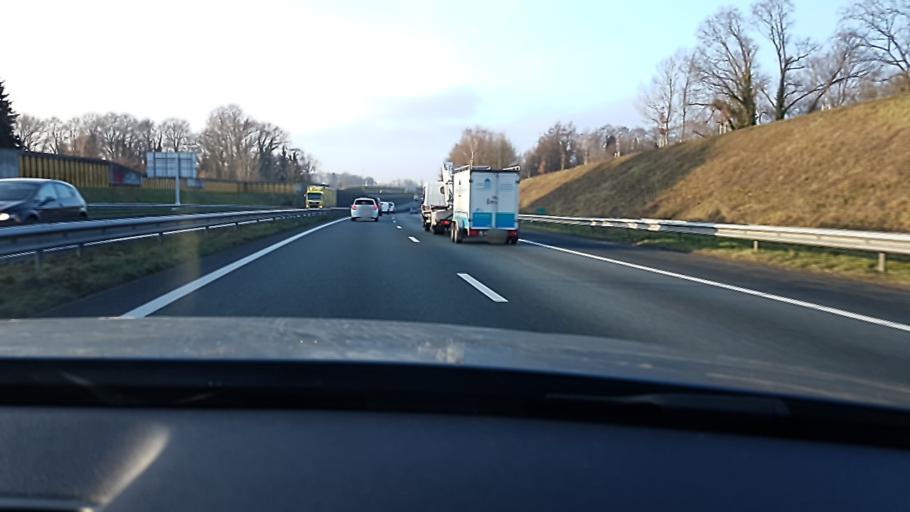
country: NL
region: Overijssel
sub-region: Gemeente Hengelo
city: Hengelo
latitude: 52.2771
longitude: 6.8268
